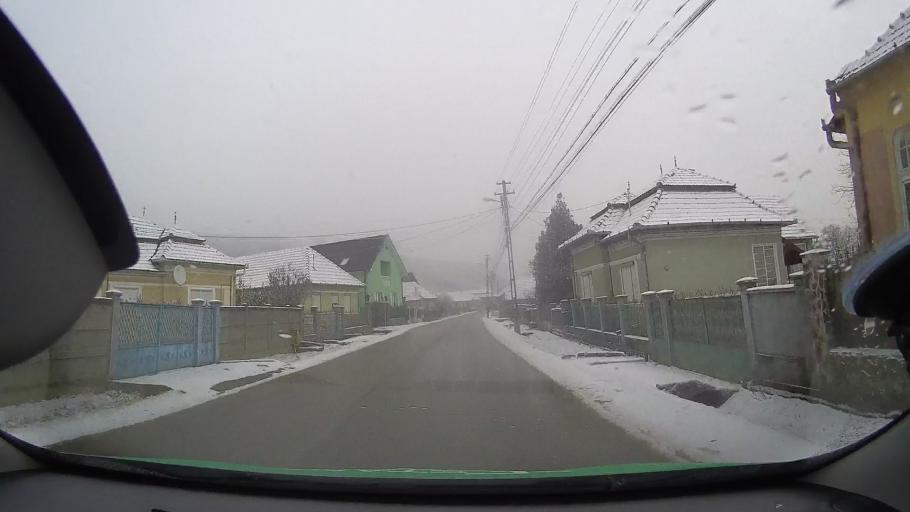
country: RO
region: Alba
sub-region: Municipiul Aiud
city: Ciumbrud
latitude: 46.3085
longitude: 23.7656
